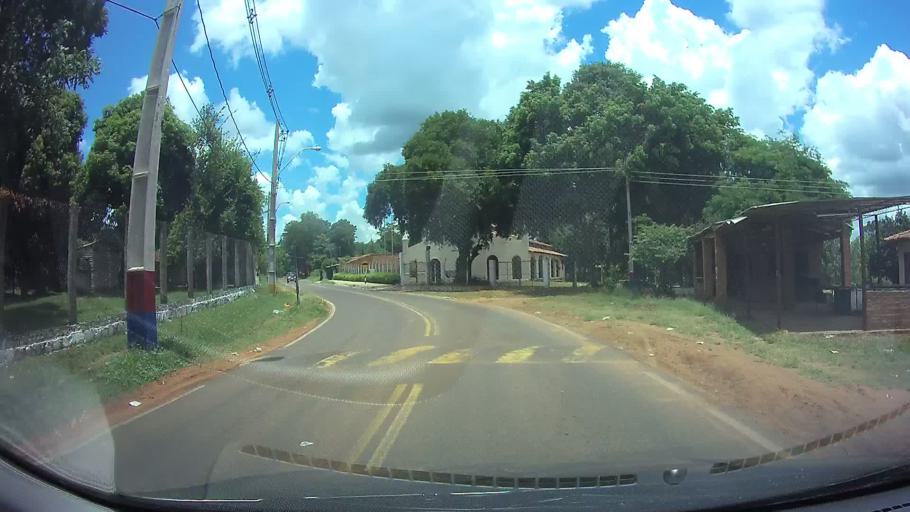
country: PY
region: Central
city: Capiata
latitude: -25.3052
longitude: -57.4403
